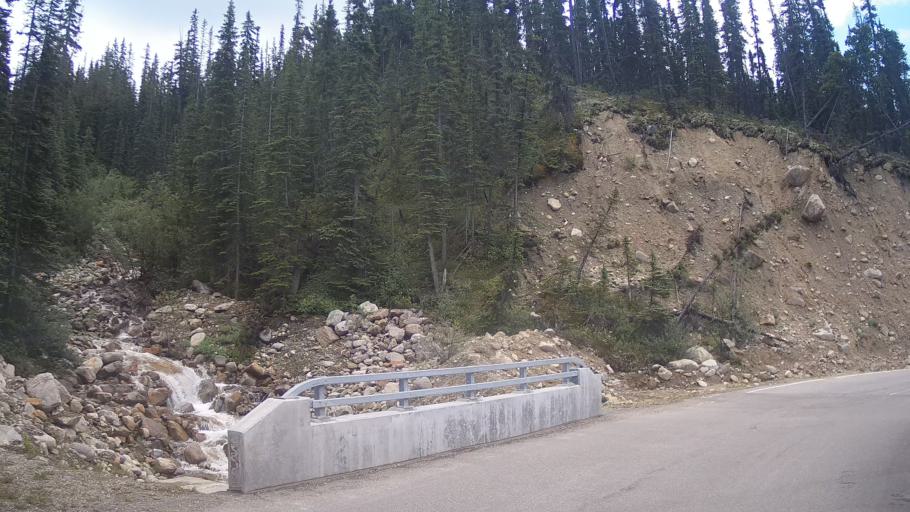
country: CA
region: Alberta
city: Jasper Park Lodge
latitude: 52.7235
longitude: -118.0506
